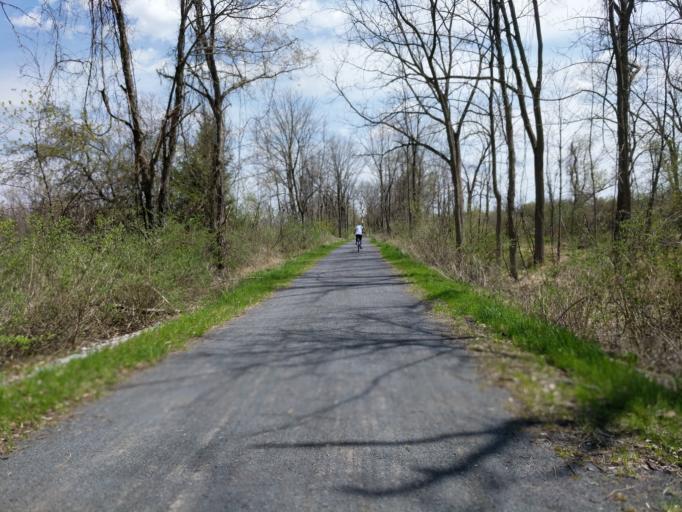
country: US
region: New York
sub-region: Tompkins County
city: Northwest Ithaca
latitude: 42.5178
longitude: -76.5725
